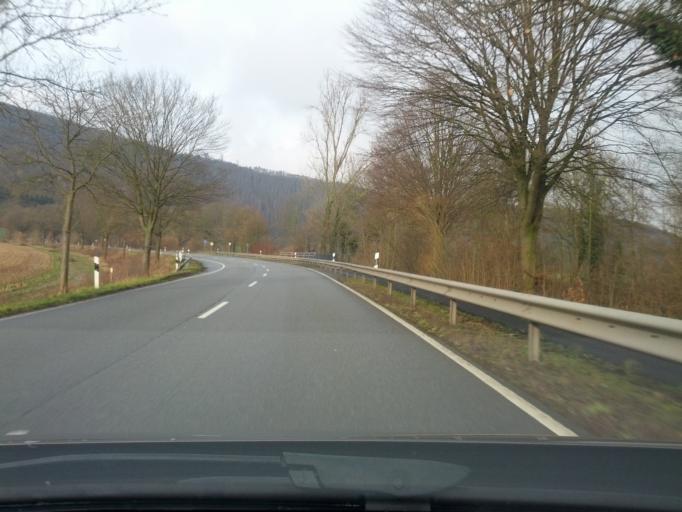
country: DE
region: Lower Saxony
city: Hannoversch Munden
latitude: 51.4493
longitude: 9.6376
